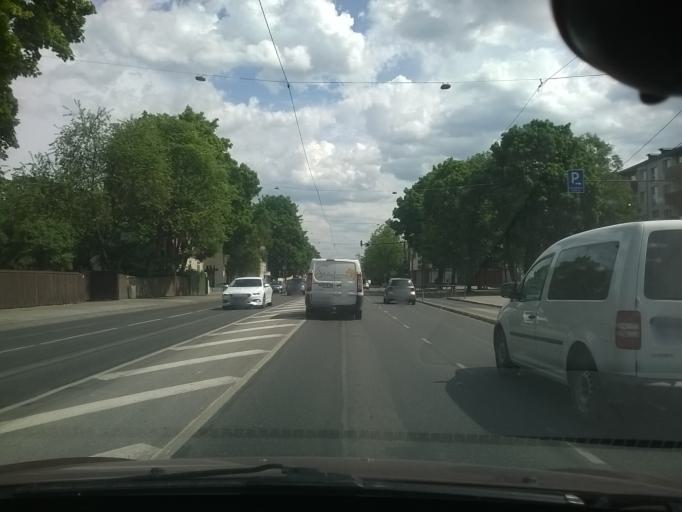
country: EE
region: Harju
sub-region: Tallinna linn
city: Tallinn
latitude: 59.4278
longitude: 24.7136
